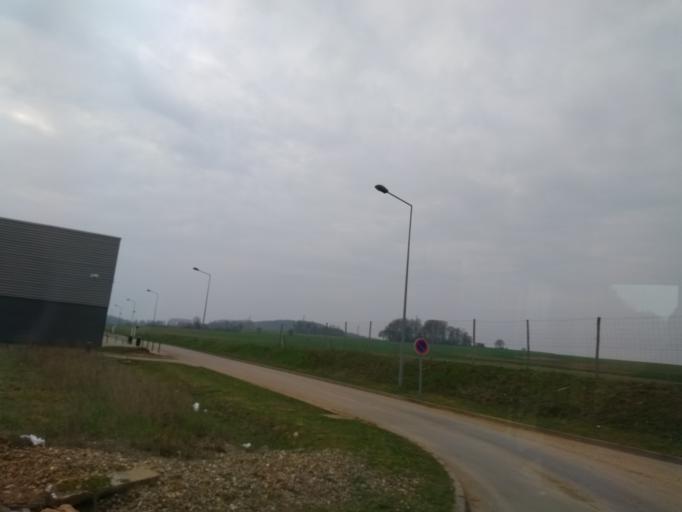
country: FR
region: Picardie
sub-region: Departement de l'Oise
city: Jaux
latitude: 49.4044
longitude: 2.7756
